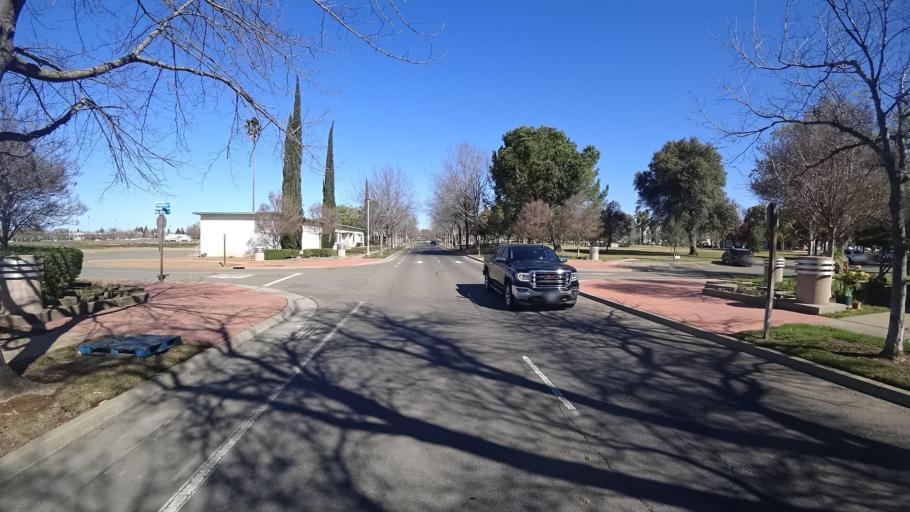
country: US
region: California
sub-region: Sacramento County
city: Rancho Cordova
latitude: 38.5677
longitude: -121.2982
